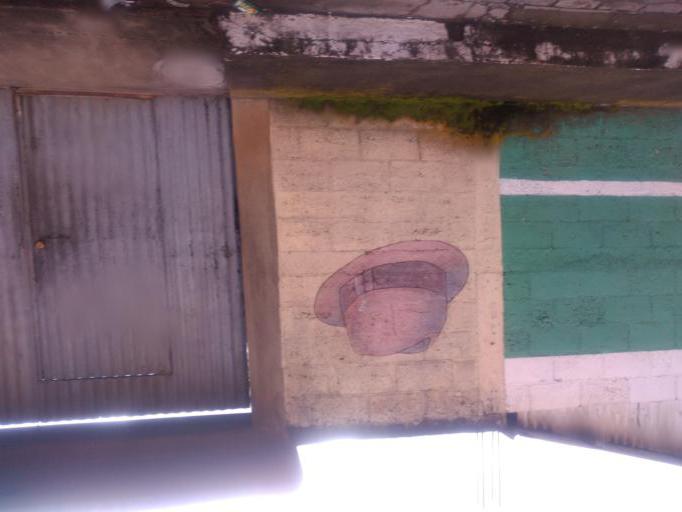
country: GT
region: Quetzaltenango
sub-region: Municipio de La Esperanza
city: La Esperanza
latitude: 14.8714
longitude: -91.5636
